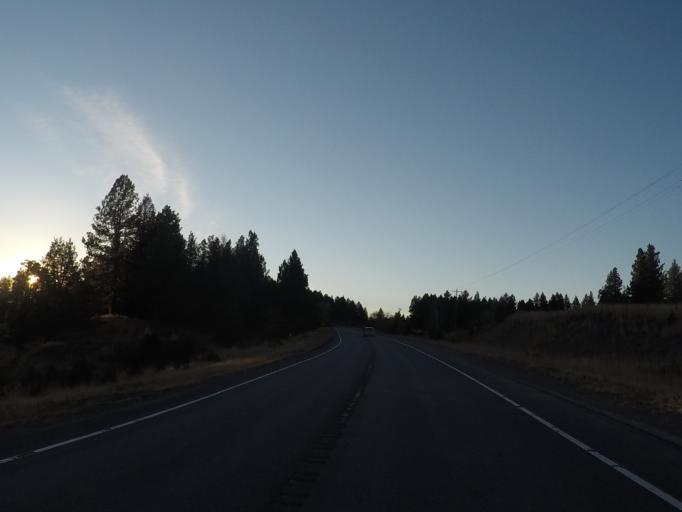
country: US
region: Montana
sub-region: Lewis and Clark County
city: Lincoln
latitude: 47.0077
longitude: -113.0519
